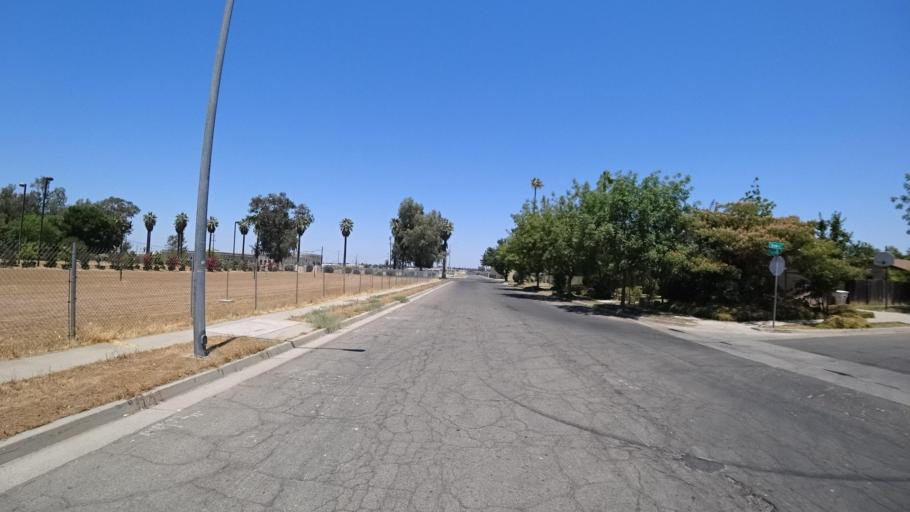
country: US
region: California
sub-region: Fresno County
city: West Park
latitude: 36.7275
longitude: -119.8221
